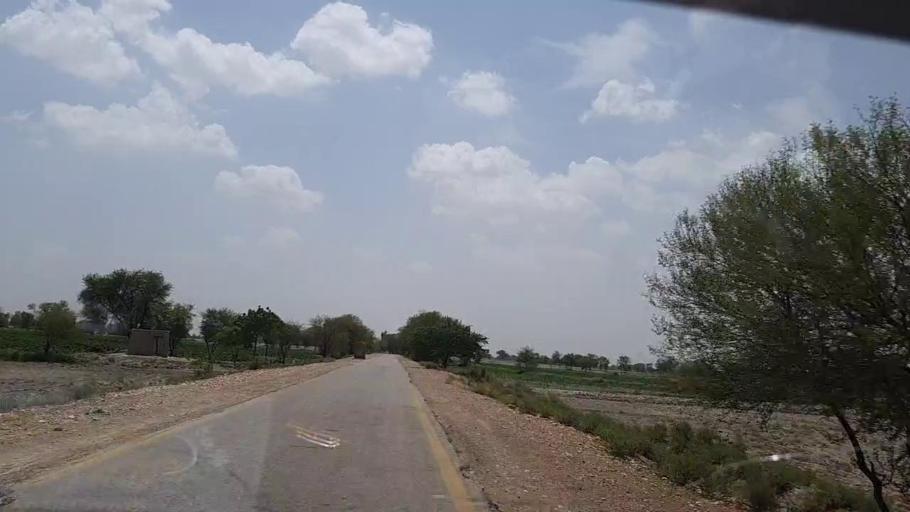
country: PK
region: Sindh
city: Bhan
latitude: 26.5410
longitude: 67.6782
